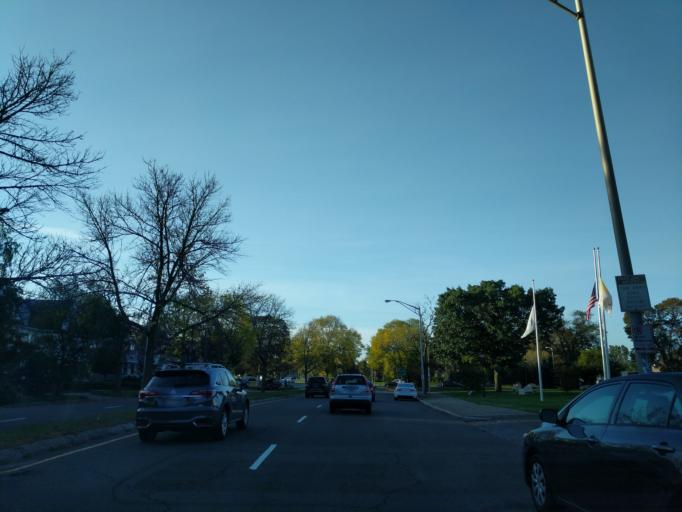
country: US
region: Massachusetts
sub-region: Middlesex County
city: Medford
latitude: 42.4245
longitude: -71.0870
